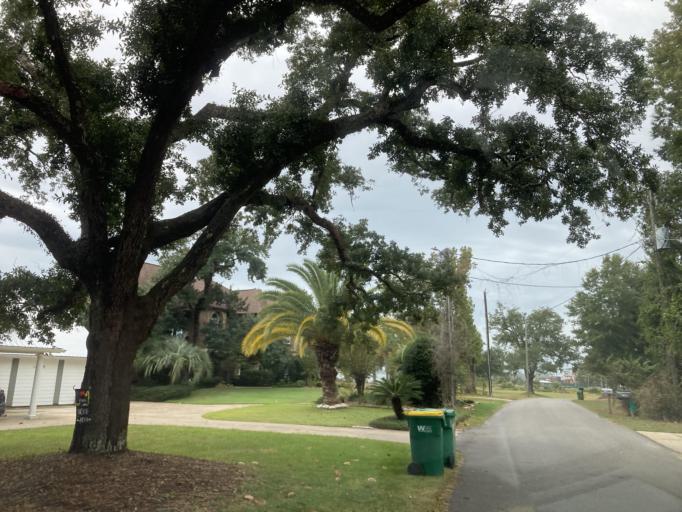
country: US
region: Mississippi
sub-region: Jackson County
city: Gulf Hills
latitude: 30.4246
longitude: -88.8366
